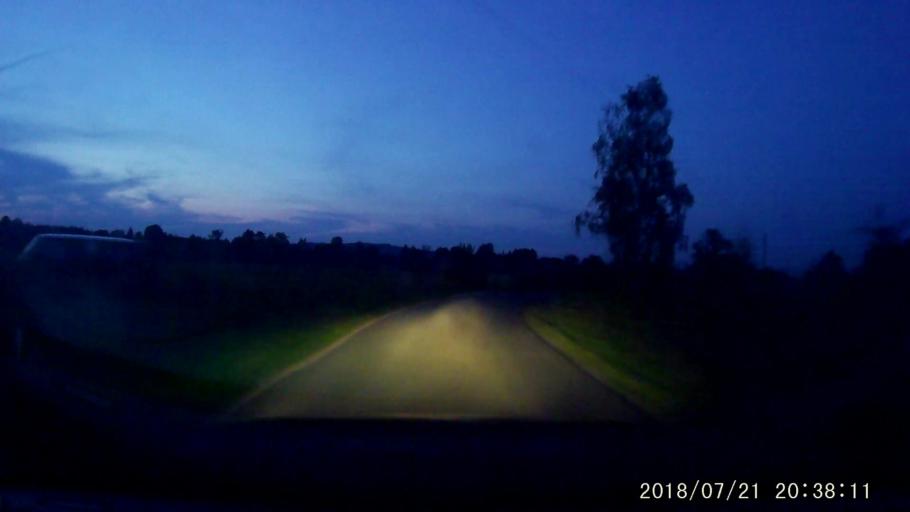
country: PL
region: Lower Silesian Voivodeship
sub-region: Powiat lubanski
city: Swieradow-Zdroj
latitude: 50.9548
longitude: 15.3105
